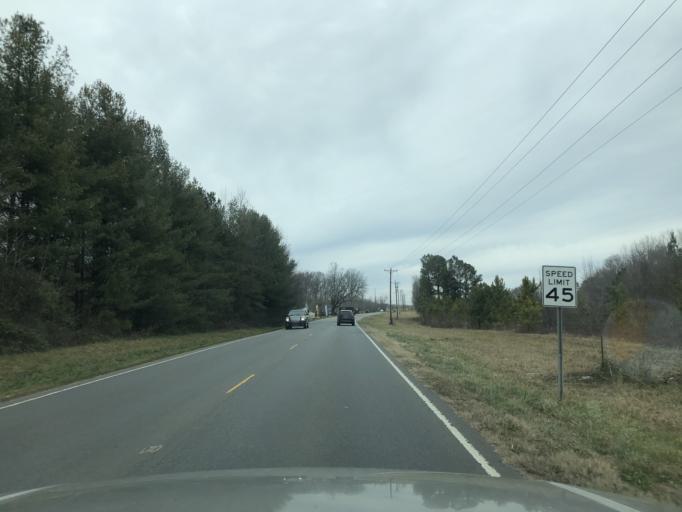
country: US
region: North Carolina
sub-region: Cleveland County
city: Shelby
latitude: 35.3058
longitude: -81.4870
